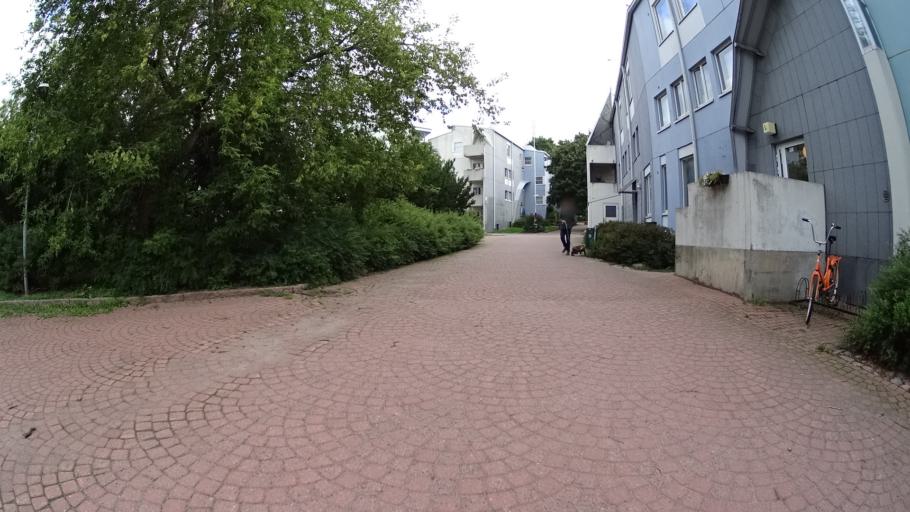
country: FI
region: Uusimaa
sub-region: Helsinki
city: Helsinki
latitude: 60.2027
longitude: 24.8960
